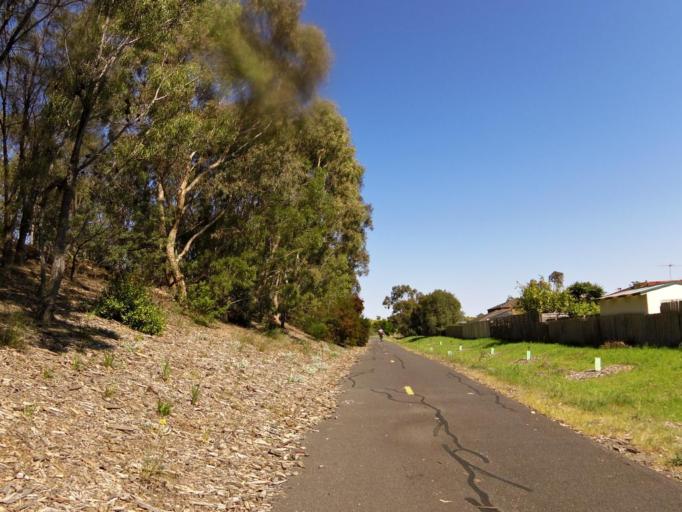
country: AU
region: Victoria
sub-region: Banyule
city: Bundoora
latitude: -37.6861
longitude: 145.0536
